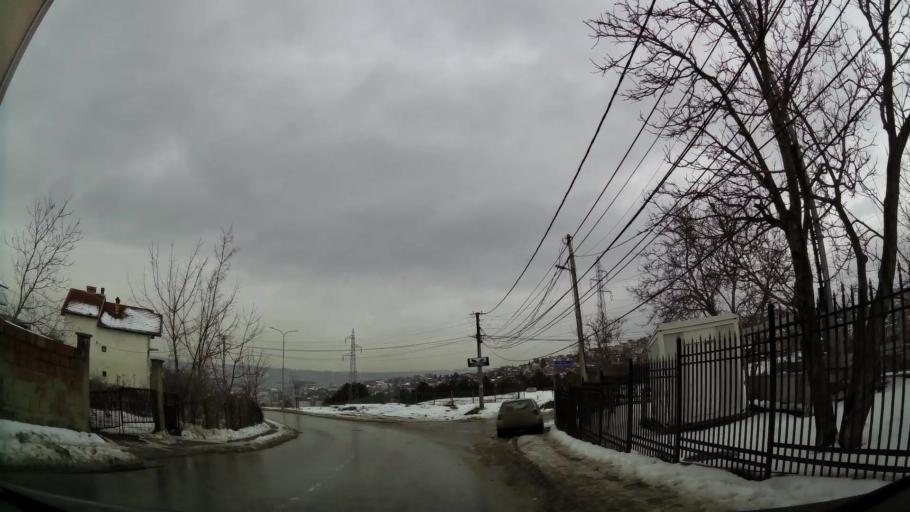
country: XK
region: Pristina
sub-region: Komuna e Prishtines
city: Pristina
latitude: 42.6630
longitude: 21.1806
